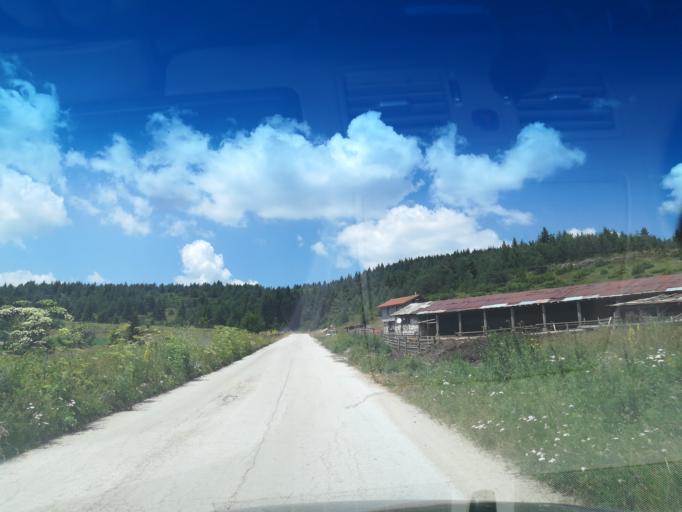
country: BG
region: Smolyan
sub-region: Obshtina Chepelare
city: Chepelare
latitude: 41.6969
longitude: 24.7808
